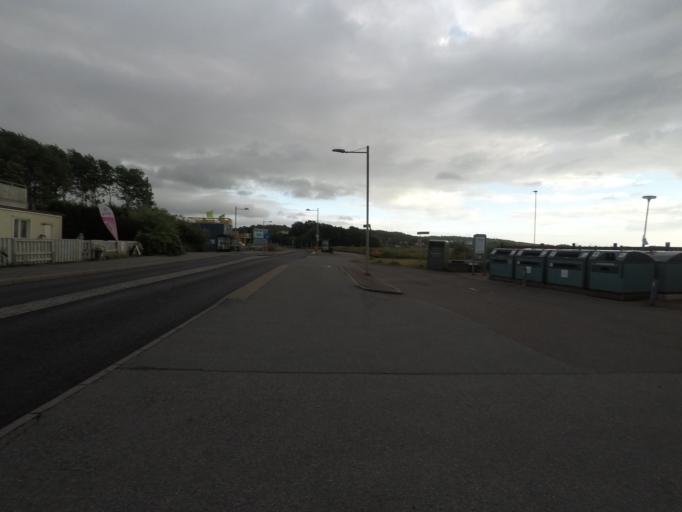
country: SE
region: Vaestra Goetaland
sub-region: Goteborg
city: Billdal
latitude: 57.5782
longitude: 11.9410
